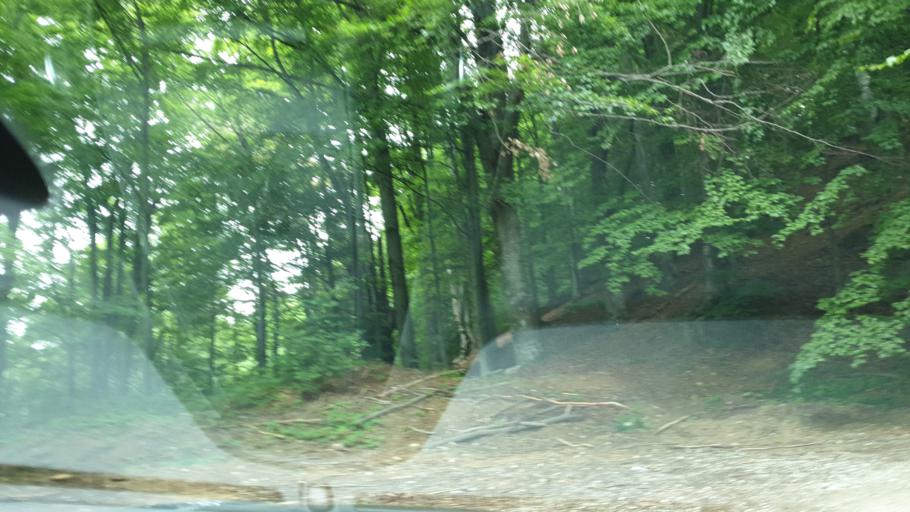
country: RO
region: Hunedoara
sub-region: Comuna Uricani
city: Uricani
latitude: 45.3078
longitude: 22.9808
